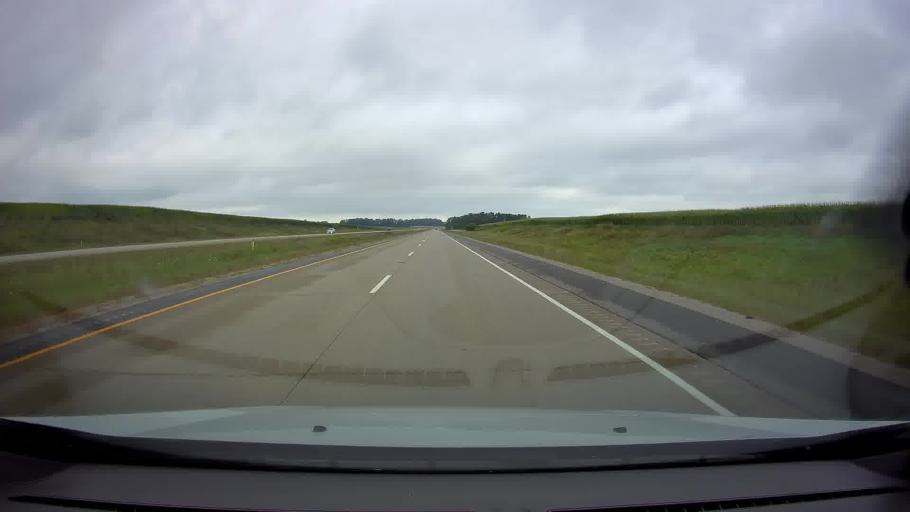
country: US
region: Wisconsin
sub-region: Brown County
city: Pulaski
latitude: 44.6480
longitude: -88.2943
